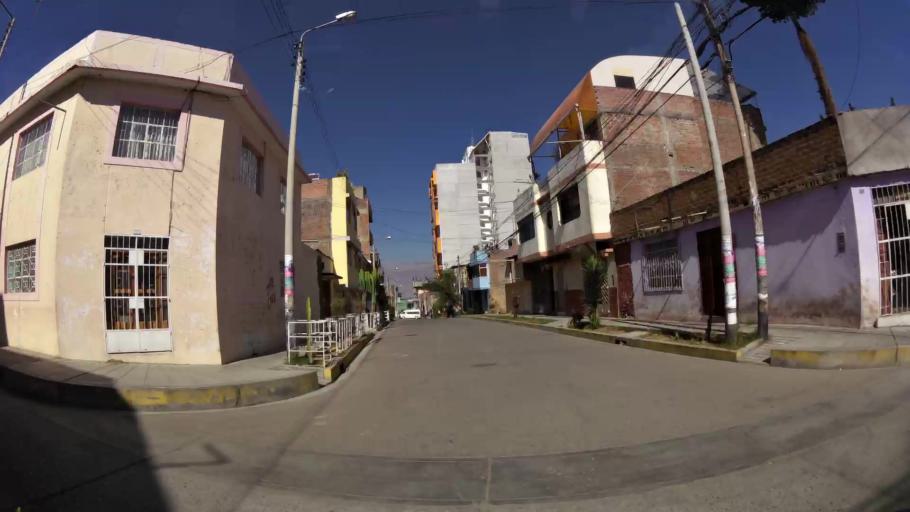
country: PE
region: Junin
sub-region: Provincia de Huancayo
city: El Tambo
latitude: -12.0557
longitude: -75.2159
